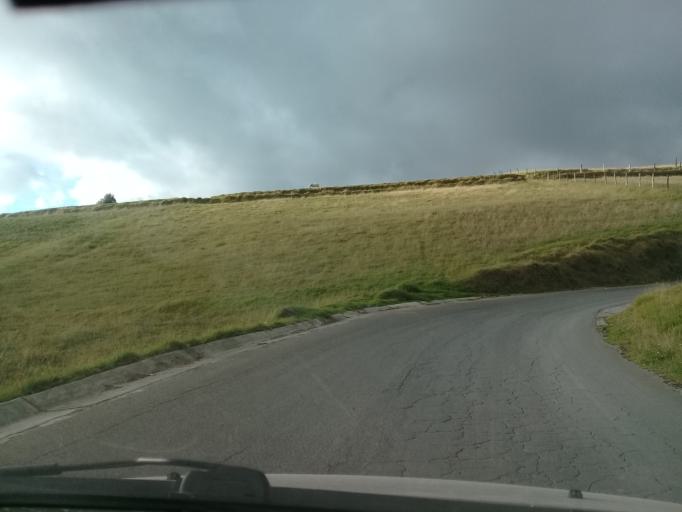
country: CO
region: Cundinamarca
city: Villapinzon
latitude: 5.2143
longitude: -73.6268
